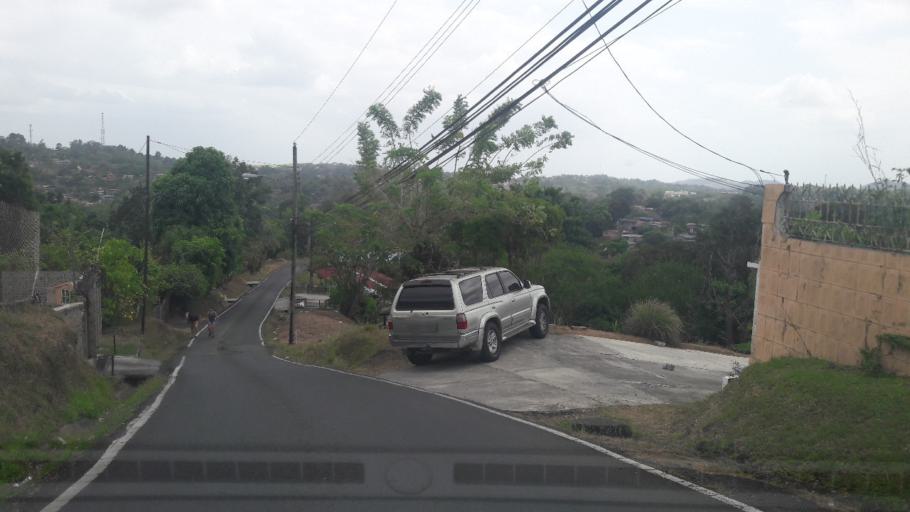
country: PA
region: Panama
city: Alcalde Diaz
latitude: 9.1245
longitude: -79.5498
